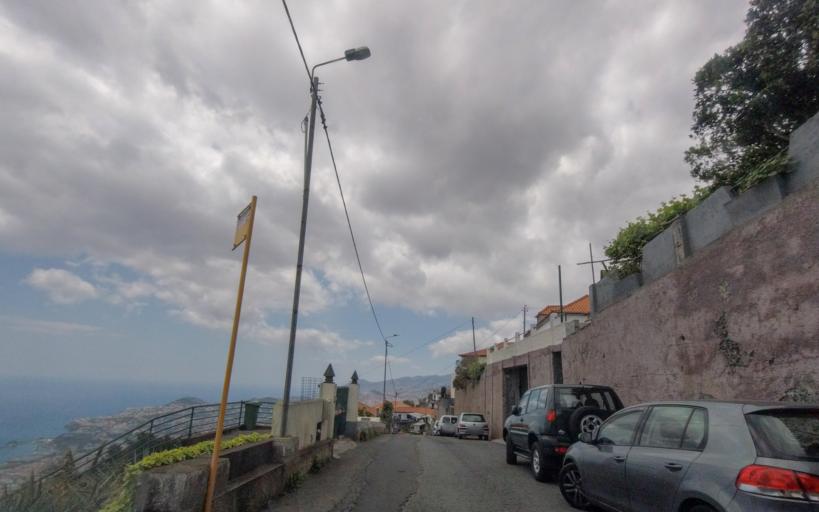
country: PT
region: Madeira
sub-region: Funchal
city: Nossa Senhora do Monte
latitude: 32.6650
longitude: -16.8804
